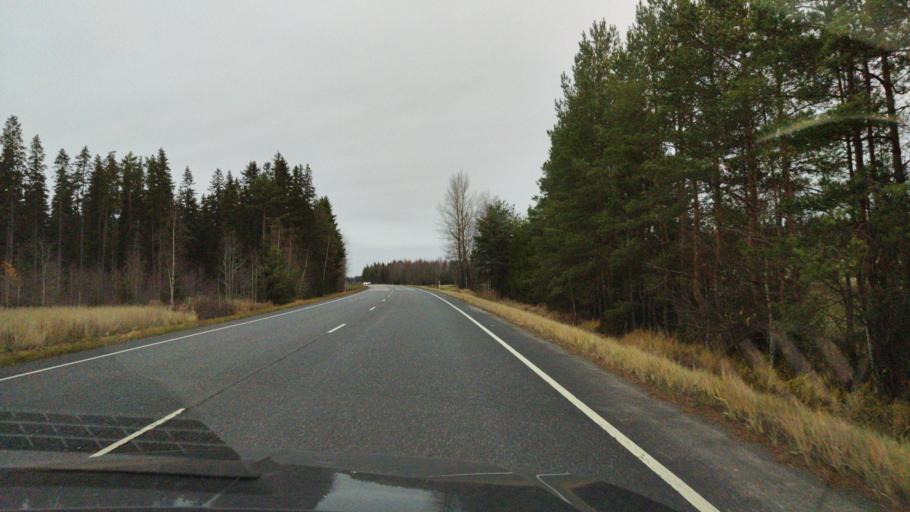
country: FI
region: Satakunta
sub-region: Rauma
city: Saekylae
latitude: 61.0023
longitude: 22.4104
